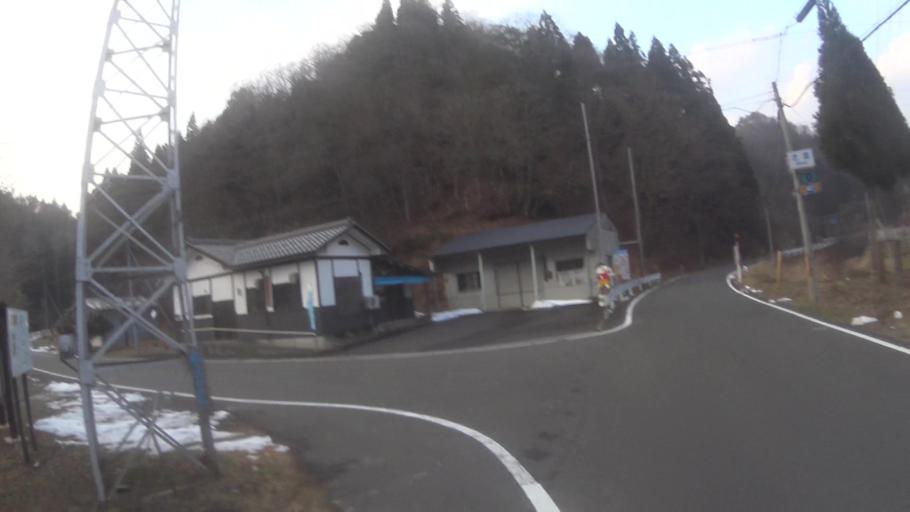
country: JP
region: Kyoto
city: Maizuru
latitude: 35.4323
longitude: 135.4785
